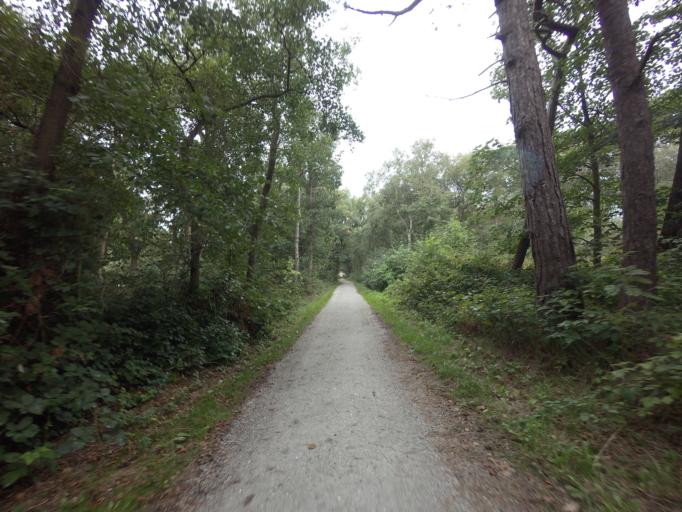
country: NL
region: Friesland
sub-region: Gemeente Schiermonnikoog
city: Schiermonnikoog
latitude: 53.4854
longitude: 6.1632
